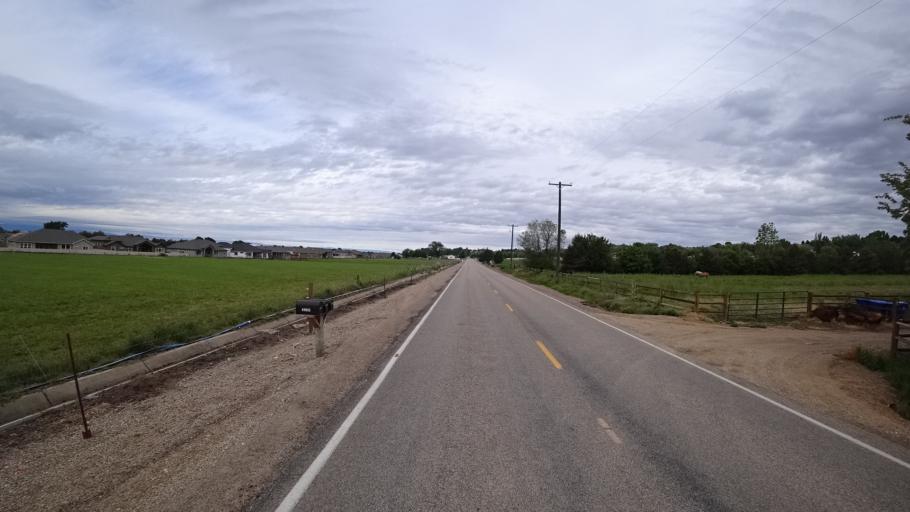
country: US
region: Idaho
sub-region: Ada County
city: Star
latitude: 43.7175
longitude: -116.5050
